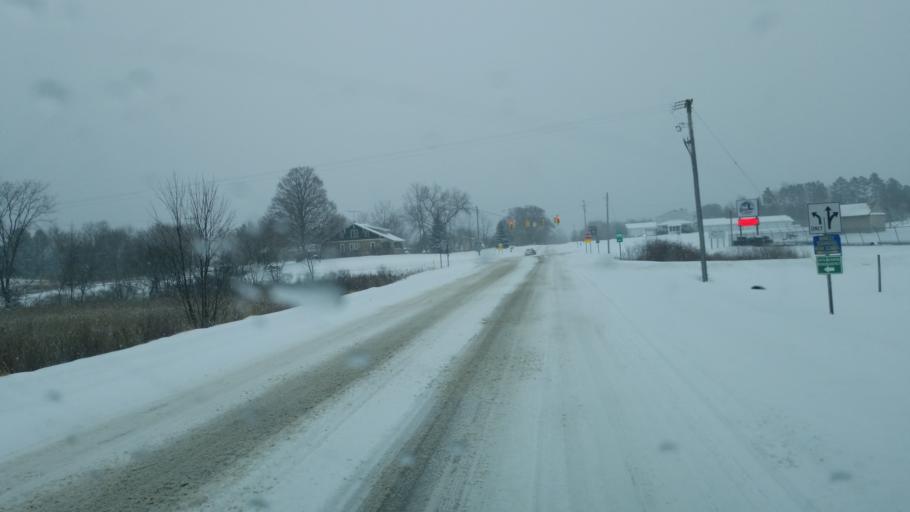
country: US
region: Michigan
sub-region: Mecosta County
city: Big Rapids
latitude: 43.5839
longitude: -85.4655
